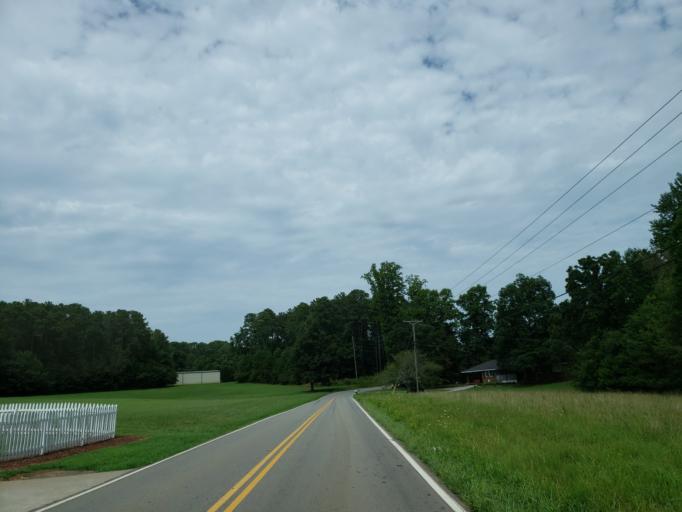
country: US
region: Georgia
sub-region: Pickens County
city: Jasper
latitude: 34.4452
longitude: -84.4257
